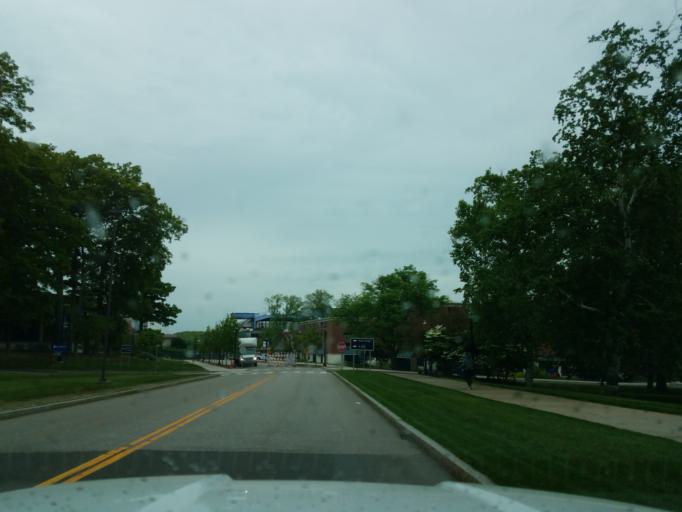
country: US
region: Connecticut
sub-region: Tolland County
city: Storrs
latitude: 41.8032
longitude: -72.2514
